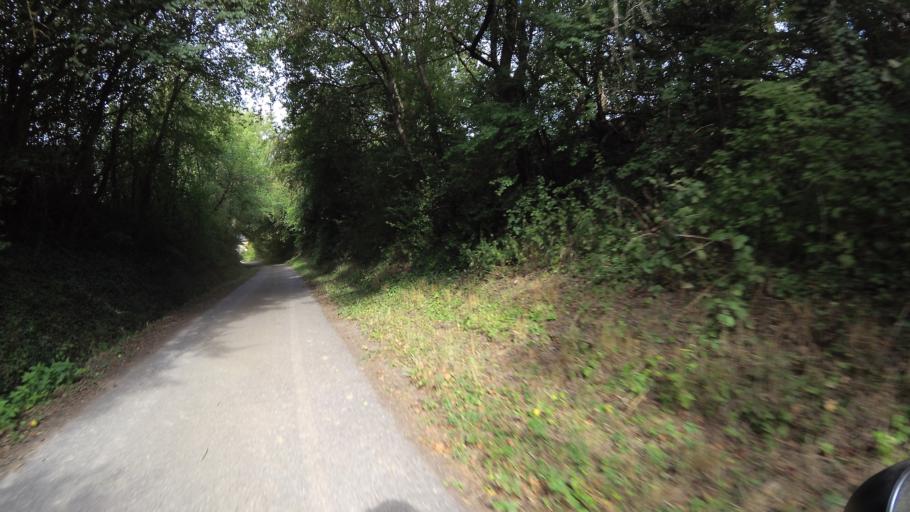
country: DE
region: Saarland
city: Gersheim
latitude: 49.1742
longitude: 7.2400
